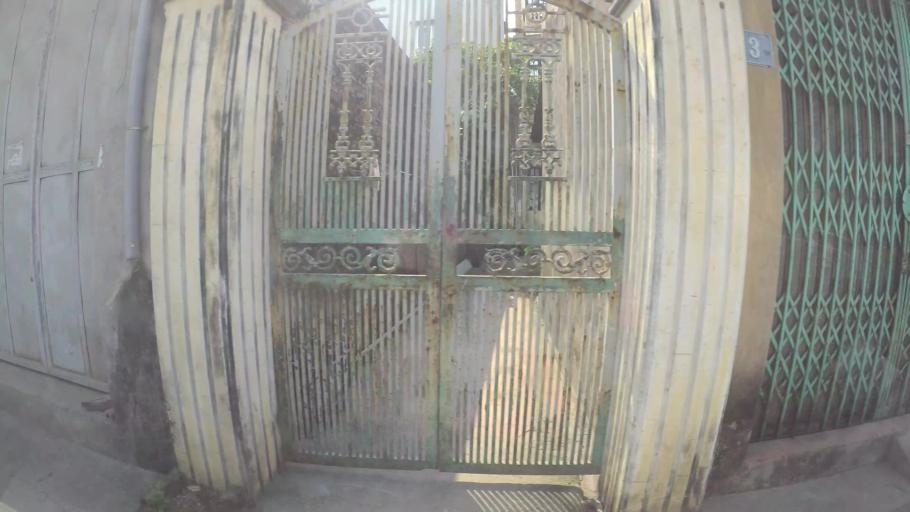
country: VN
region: Ha Noi
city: Ha Dong
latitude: 21.0004
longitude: 105.7573
